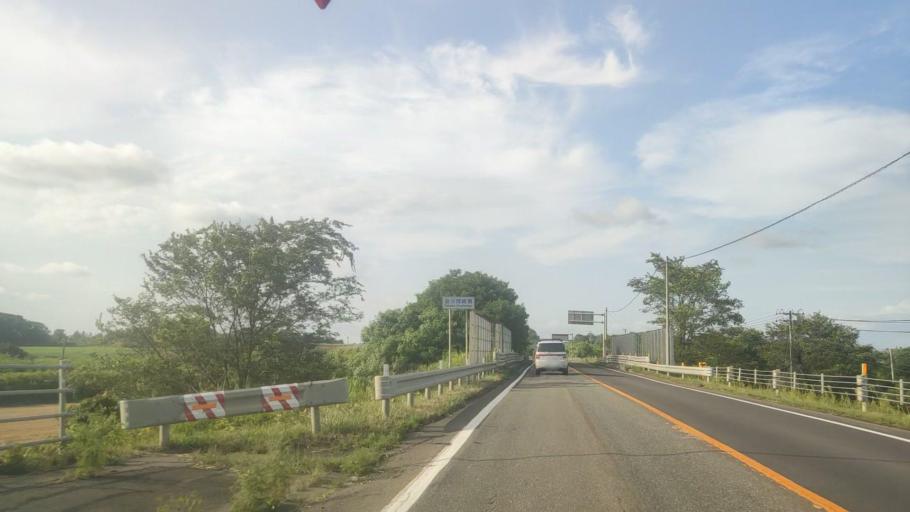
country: JP
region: Hokkaido
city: Chitose
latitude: 42.8881
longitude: 141.8124
